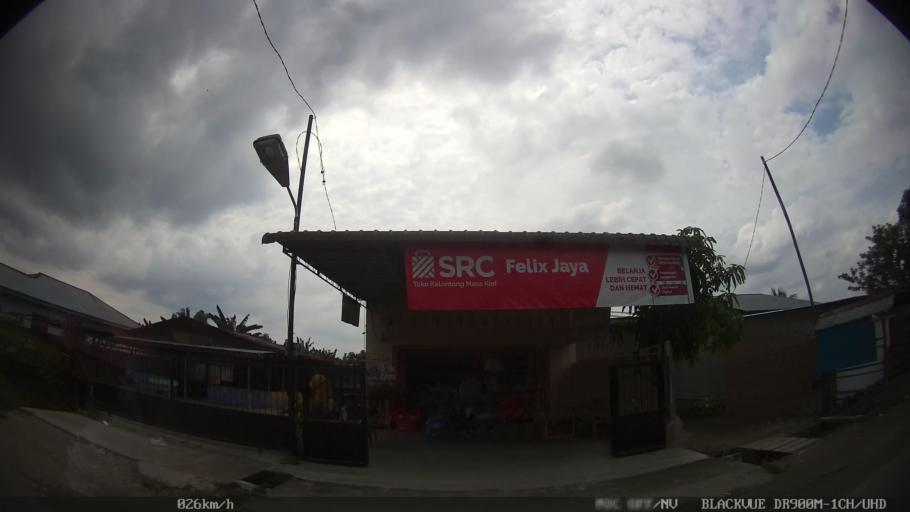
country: ID
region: North Sumatra
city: Sunggal
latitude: 3.6249
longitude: 98.6060
